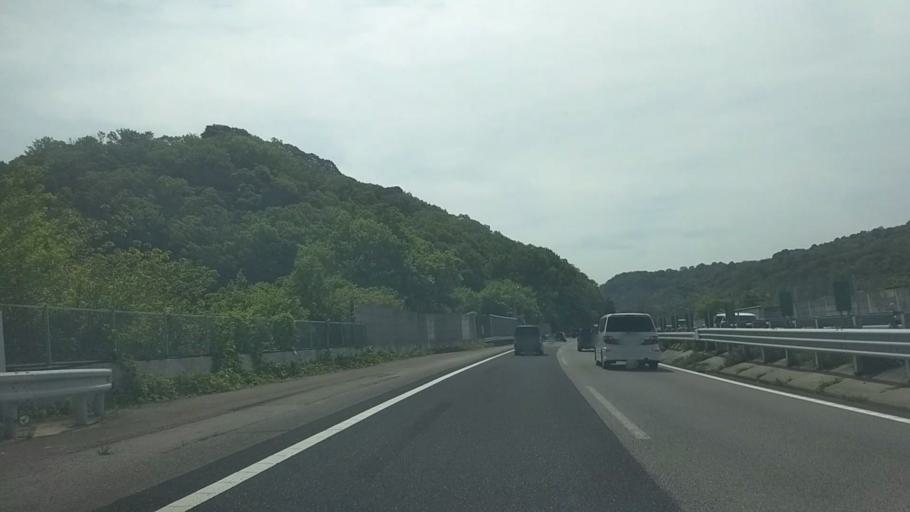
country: JP
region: Aichi
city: Okazaki
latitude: 34.9317
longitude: 137.2203
